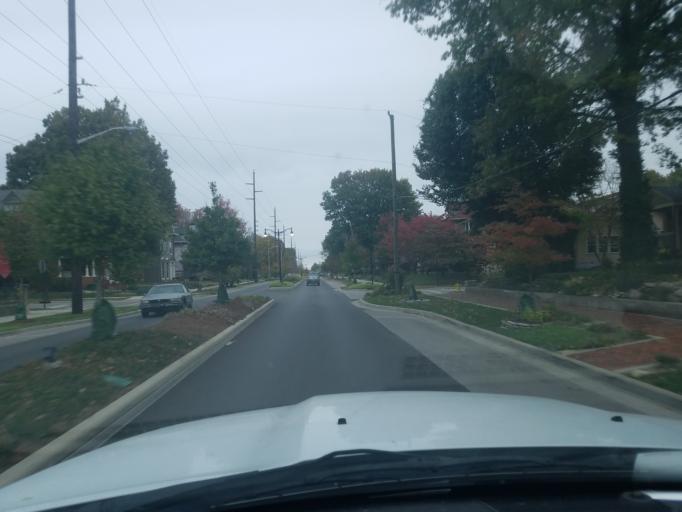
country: US
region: Indiana
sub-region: Floyd County
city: New Albany
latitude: 38.2870
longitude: -85.8120
